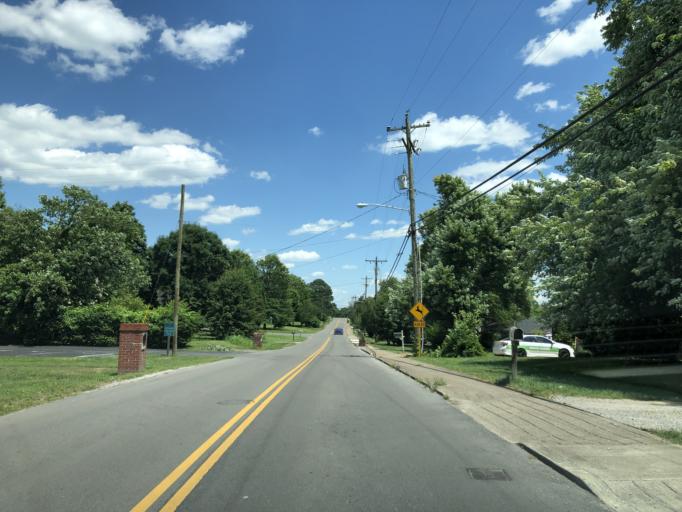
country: US
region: Tennessee
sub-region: Davidson County
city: Nashville
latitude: 36.1865
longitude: -86.7168
